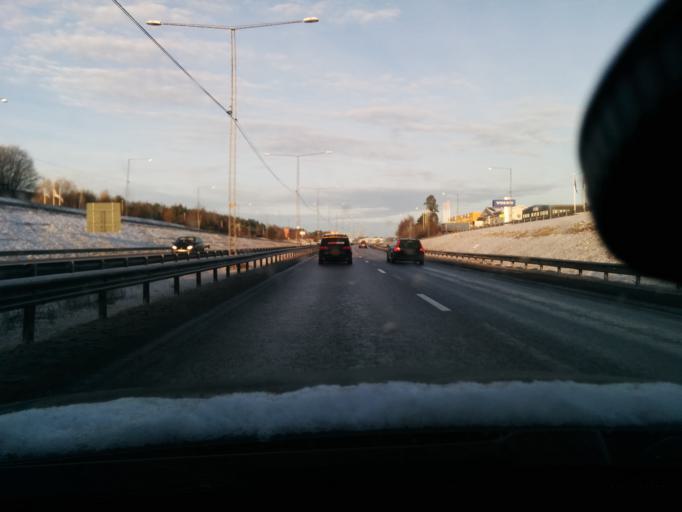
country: SE
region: Stockholm
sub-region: Upplands Vasby Kommun
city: Upplands Vaesby
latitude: 59.5152
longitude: 17.9244
